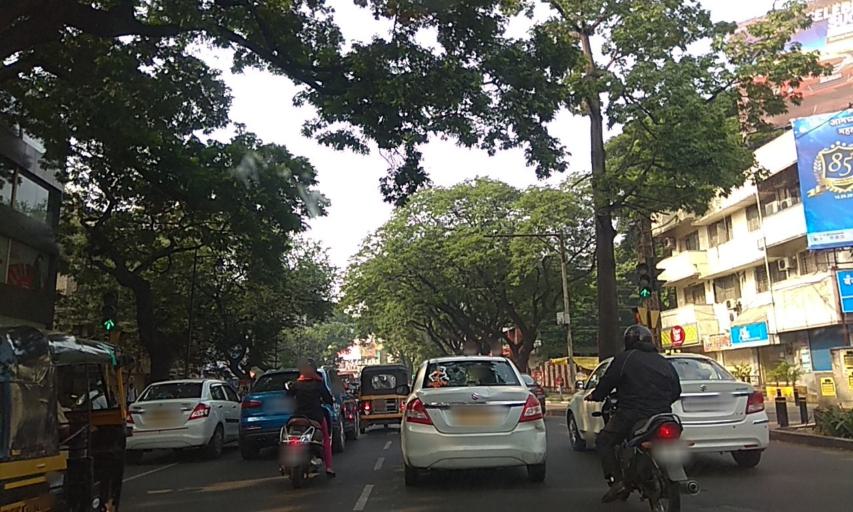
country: IN
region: Maharashtra
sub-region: Pune Division
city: Pune
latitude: 18.5173
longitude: 73.8434
